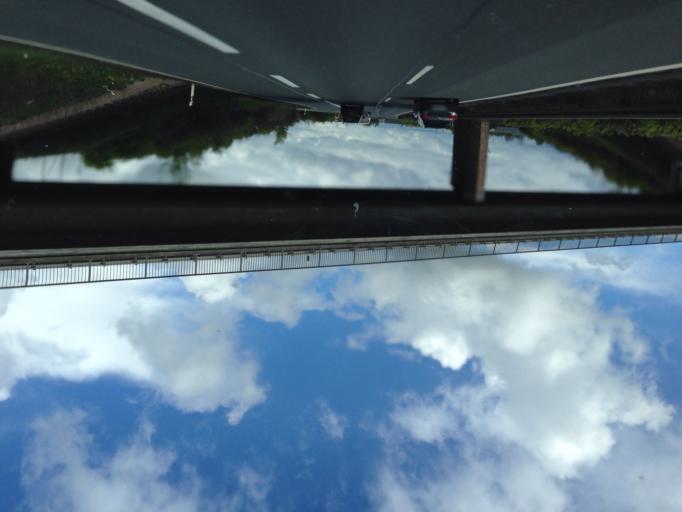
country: DE
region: Saxony-Anhalt
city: Oppin
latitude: 51.5551
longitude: 12.0063
